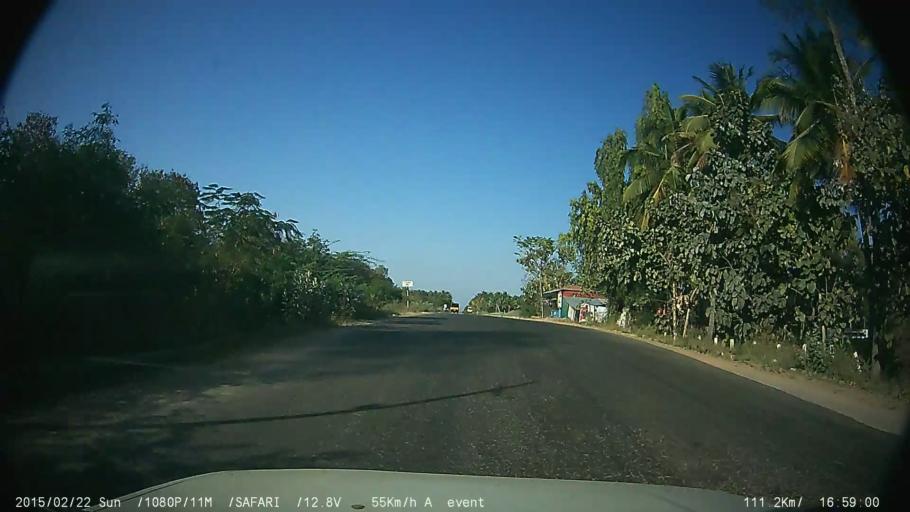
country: IN
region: Tamil Nadu
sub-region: Theni
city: Gudalur
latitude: 9.6907
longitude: 77.2535
